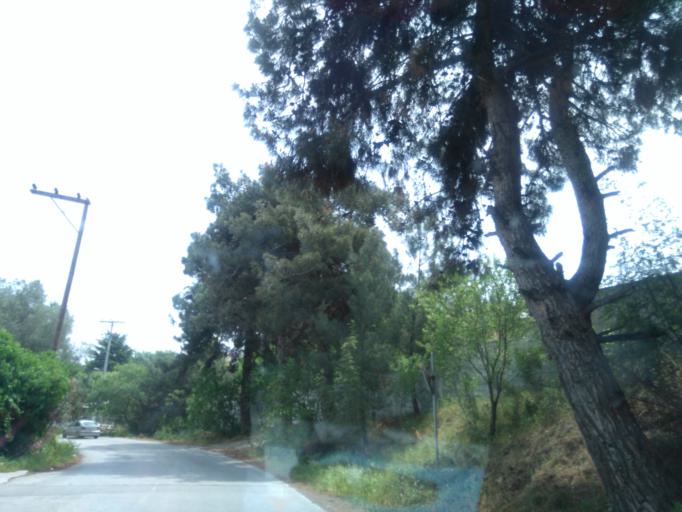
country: GR
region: Central Macedonia
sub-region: Nomos Thessalonikis
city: Lagyna
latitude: 40.7251
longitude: 22.9927
